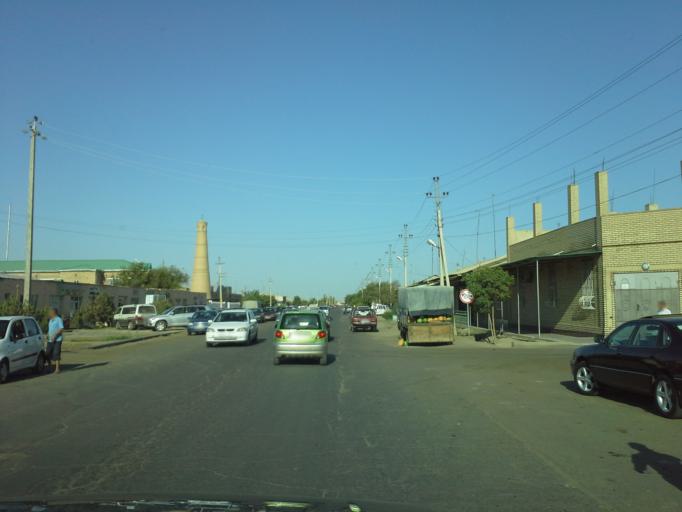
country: TM
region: Dasoguz
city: Dasoguz
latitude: 41.8317
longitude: 59.9842
